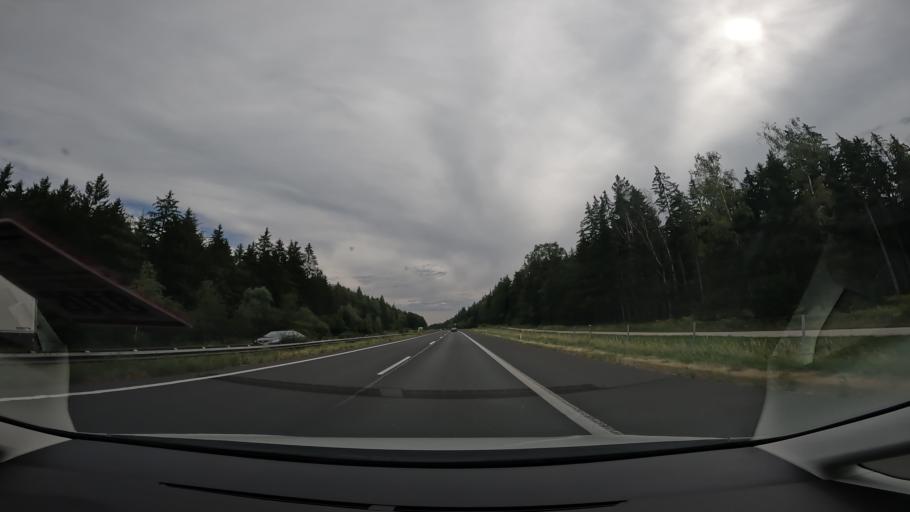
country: AT
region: Styria
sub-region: Politischer Bezirk Hartberg-Fuerstenfeld
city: Bad Waltersdorf
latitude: 47.1315
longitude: 15.9810
